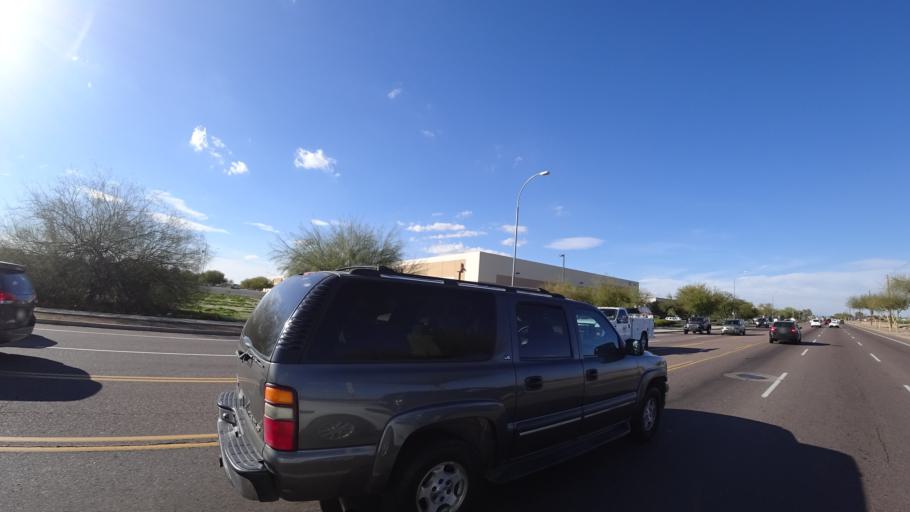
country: US
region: Arizona
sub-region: Maricopa County
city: Tolleson
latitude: 33.4530
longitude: -112.2383
